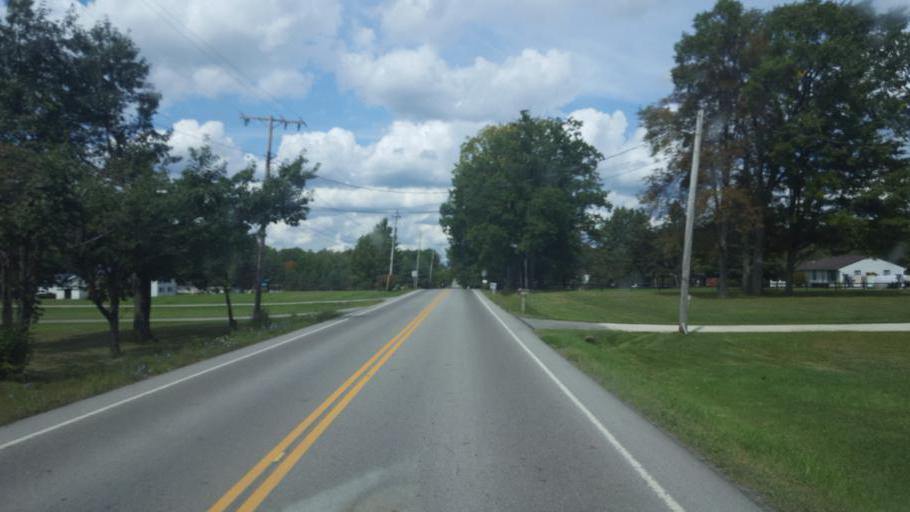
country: US
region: Ohio
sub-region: Geauga County
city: Middlefield
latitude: 41.4185
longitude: -81.0387
